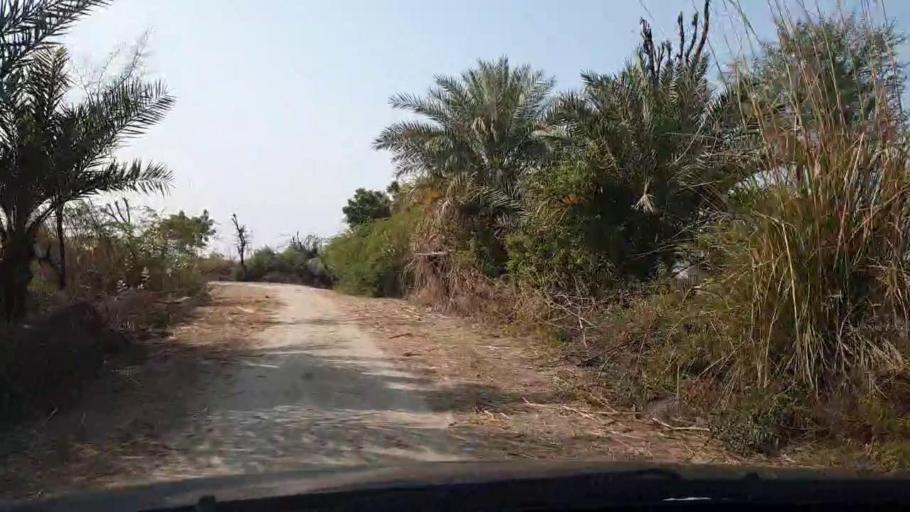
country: PK
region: Sindh
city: Sanghar
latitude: 26.0194
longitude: 68.9062
